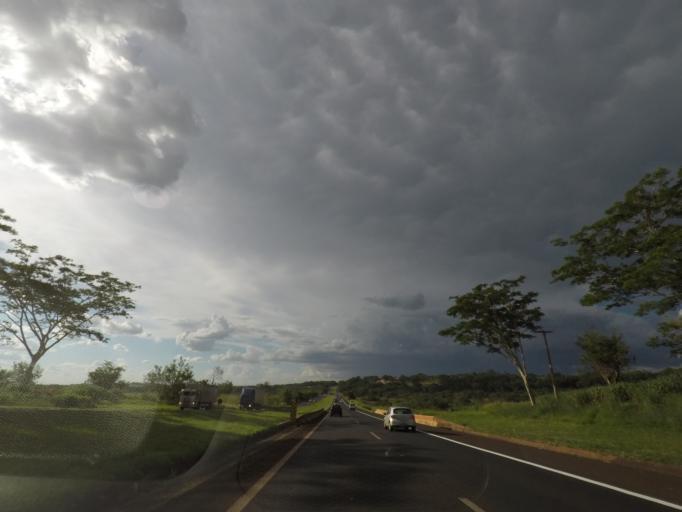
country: BR
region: Sao Paulo
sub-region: Jardinopolis
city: Jardinopolis
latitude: -21.0719
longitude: -47.8101
